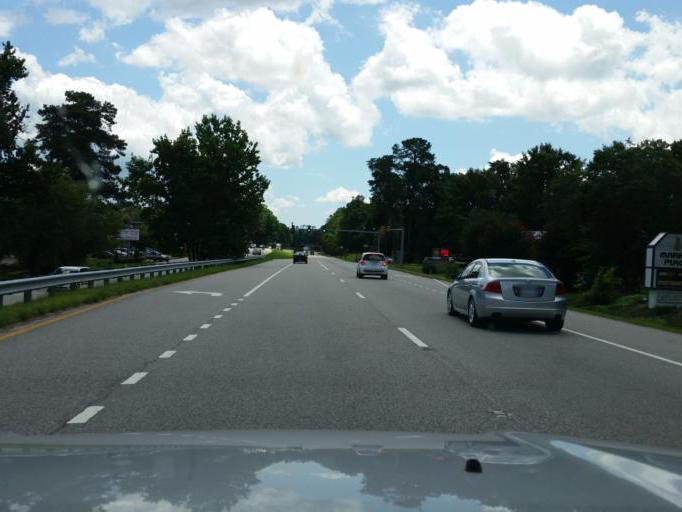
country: US
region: Virginia
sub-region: City of Williamsburg
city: Williamsburg
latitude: 37.2473
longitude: -76.6589
